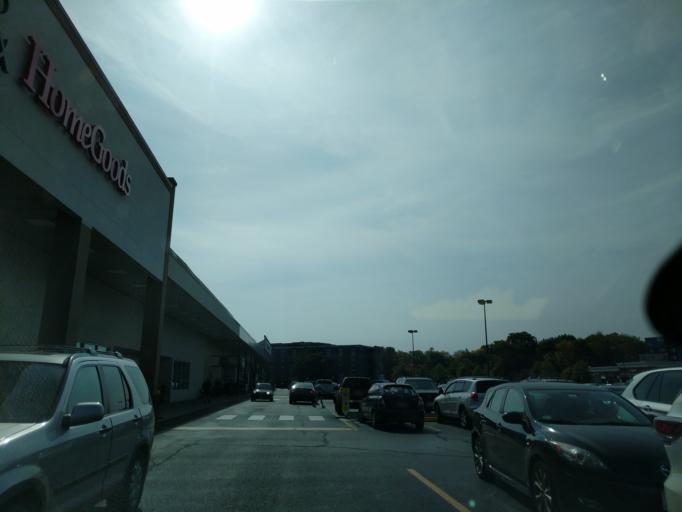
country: US
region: Massachusetts
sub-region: Middlesex County
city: Arlington
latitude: 42.3901
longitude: -71.1410
